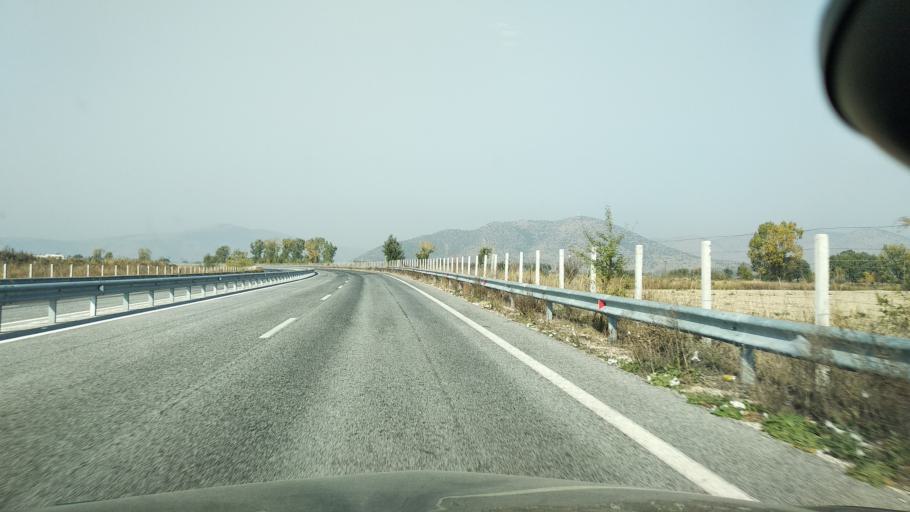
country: GR
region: Thessaly
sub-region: Trikala
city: Farkadona
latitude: 39.5845
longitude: 22.0459
